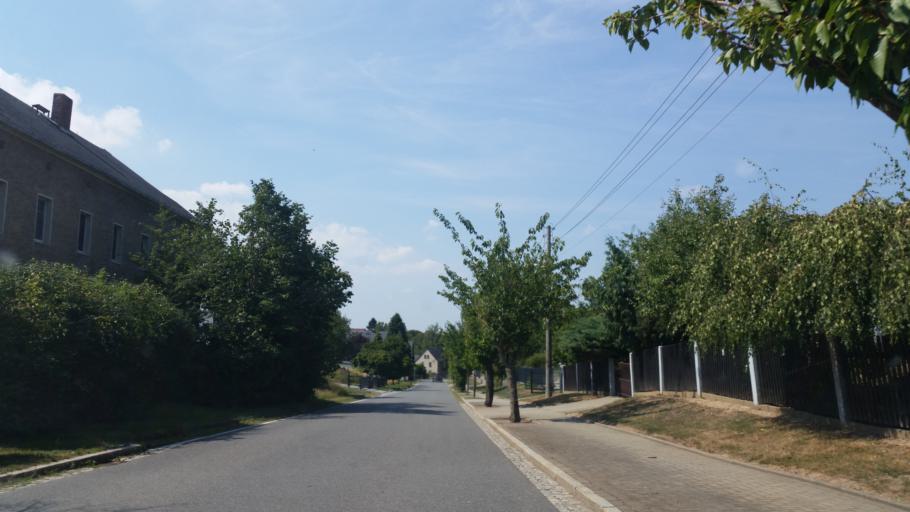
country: DE
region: Saxony
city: Wilsdruff
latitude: 51.0679
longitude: 13.5422
